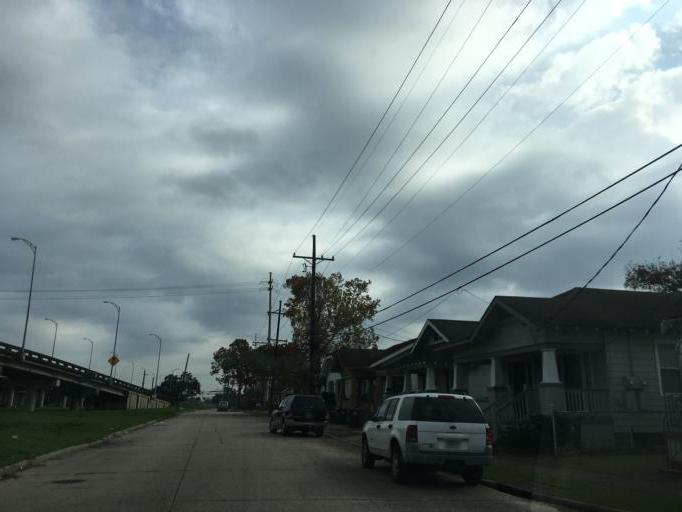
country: US
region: Louisiana
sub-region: Orleans Parish
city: New Orleans
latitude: 29.9907
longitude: -90.0610
